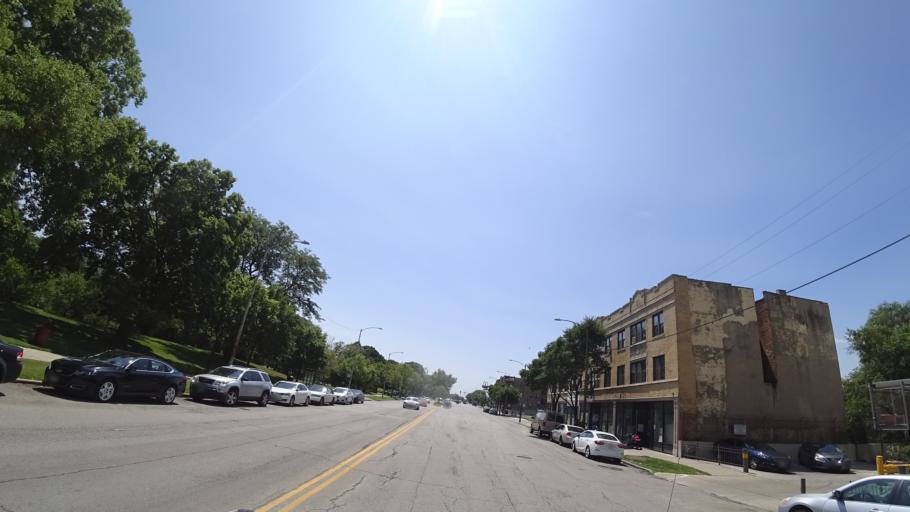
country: US
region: Illinois
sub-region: Cook County
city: Chicago
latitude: 41.7777
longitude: -87.5863
